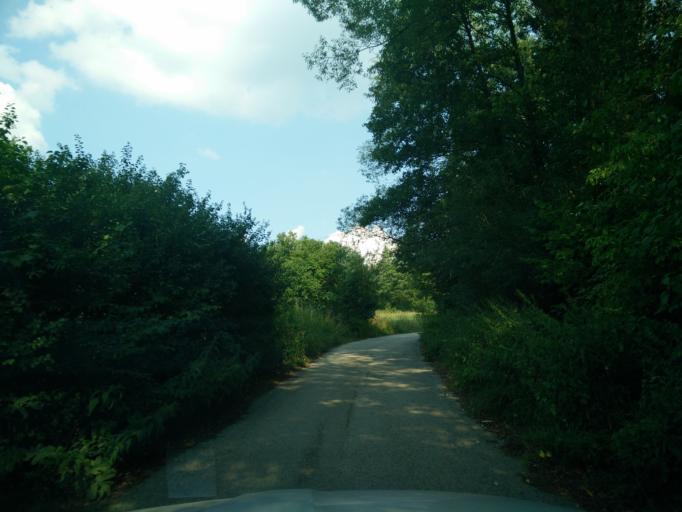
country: SK
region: Nitriansky
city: Prievidza
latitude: 48.7541
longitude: 18.6279
